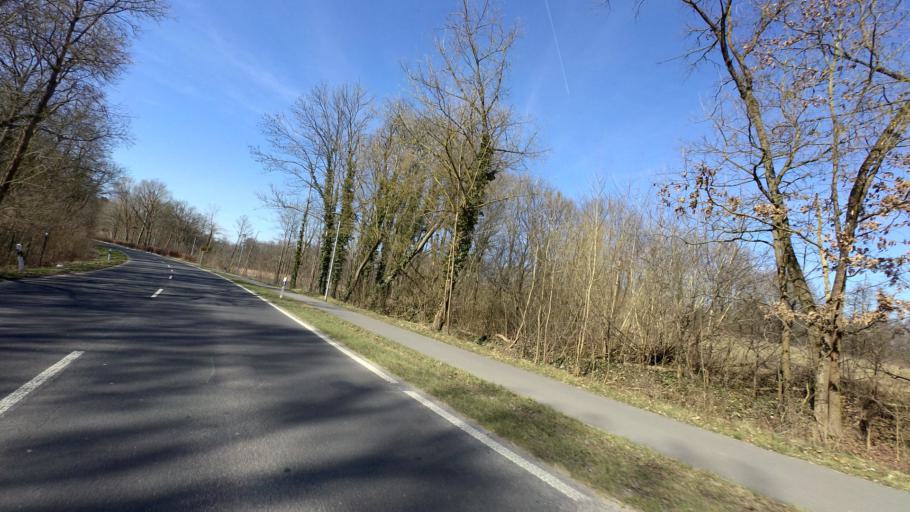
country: DE
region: Brandenburg
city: Muncheberg
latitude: 52.5208
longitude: 14.1075
